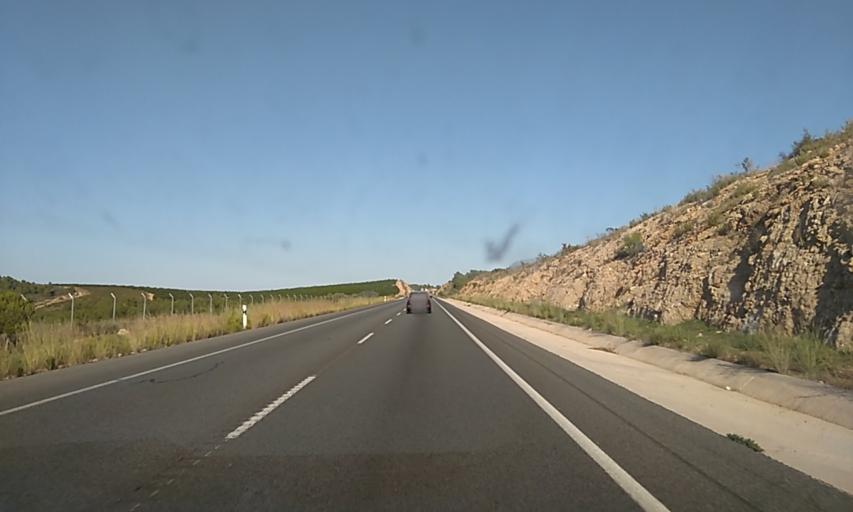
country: ES
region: Valencia
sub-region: Provincia de Castello
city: Torreblanca
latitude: 40.2126
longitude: 0.1462
